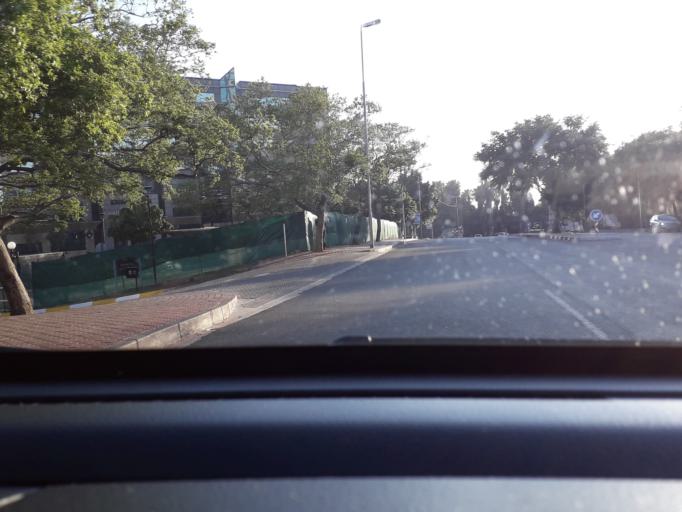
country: ZA
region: Gauteng
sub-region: City of Johannesburg Metropolitan Municipality
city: Johannesburg
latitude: -26.1010
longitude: 28.0569
